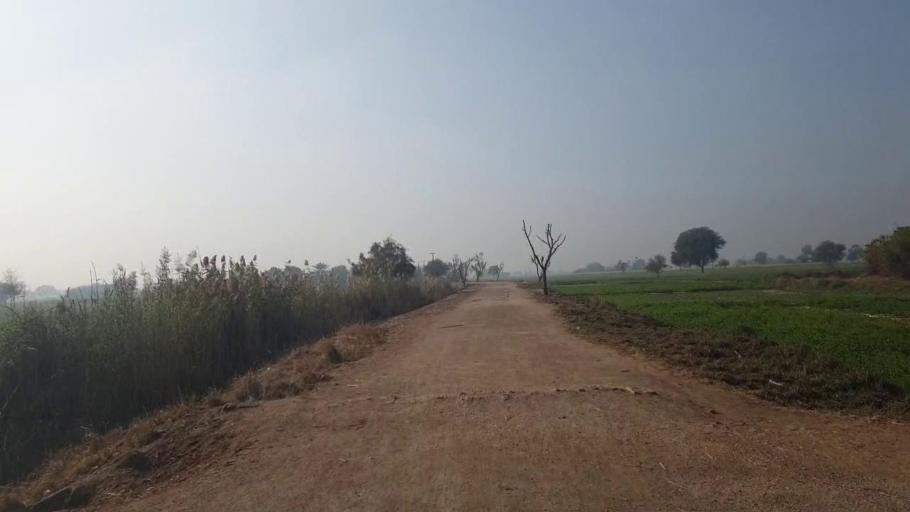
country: PK
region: Sindh
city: Shahdadpur
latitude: 25.9413
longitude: 68.5759
